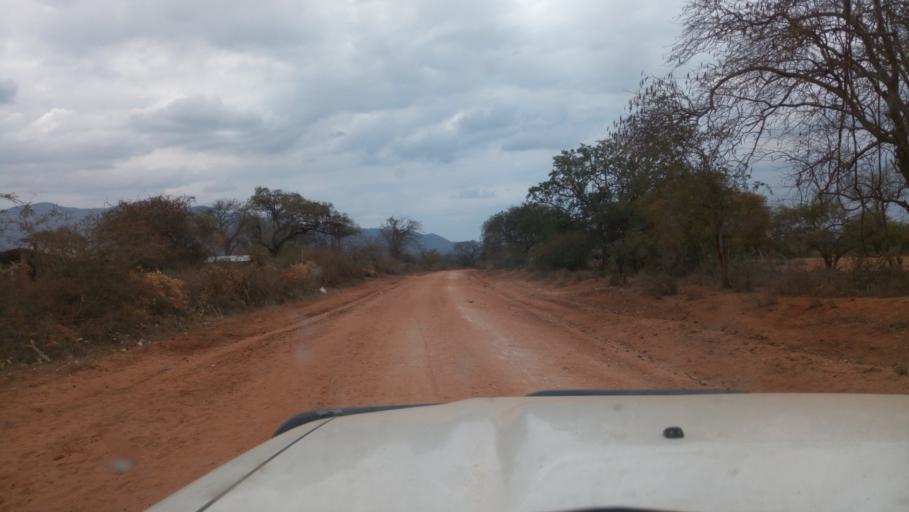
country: KE
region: Kitui
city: Kitui
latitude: -1.8519
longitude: 38.4226
